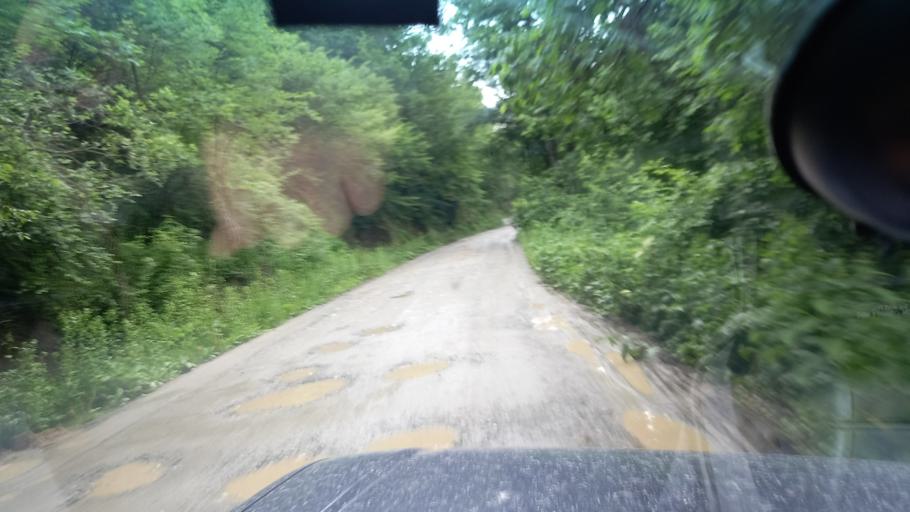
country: RU
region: Krasnodarskiy
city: Psebay
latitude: 44.0386
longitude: 40.7528
